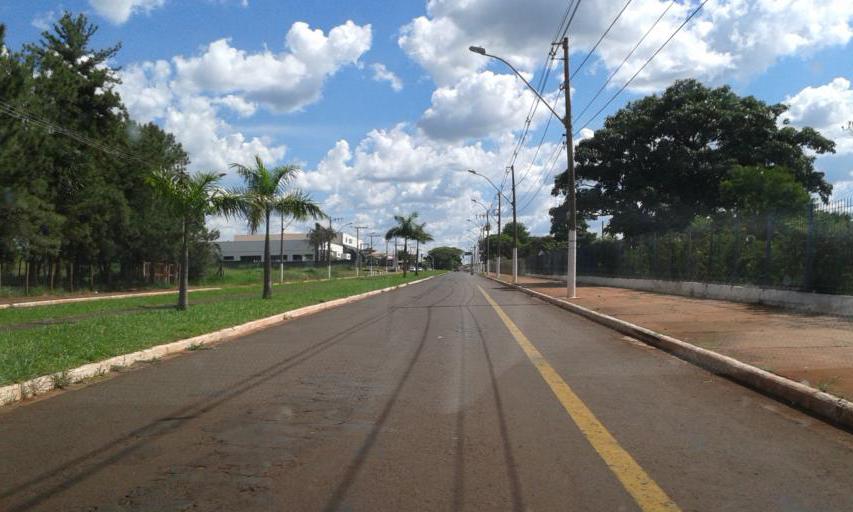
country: BR
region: Minas Gerais
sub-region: Ituiutaba
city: Ituiutaba
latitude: -18.9732
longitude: -49.4814
